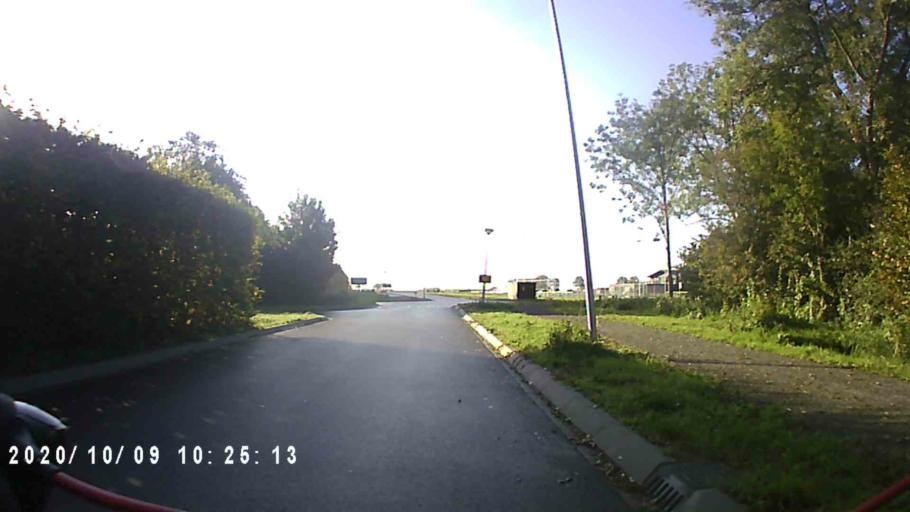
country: NL
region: Groningen
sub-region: Gemeente Winsum
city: Winsum
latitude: 53.3285
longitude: 6.5105
